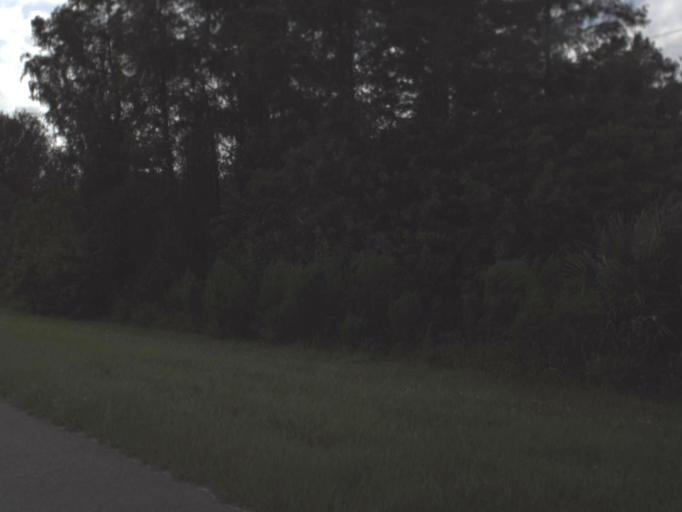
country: US
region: Florida
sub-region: Collier County
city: Immokalee
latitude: 26.3566
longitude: -81.3438
